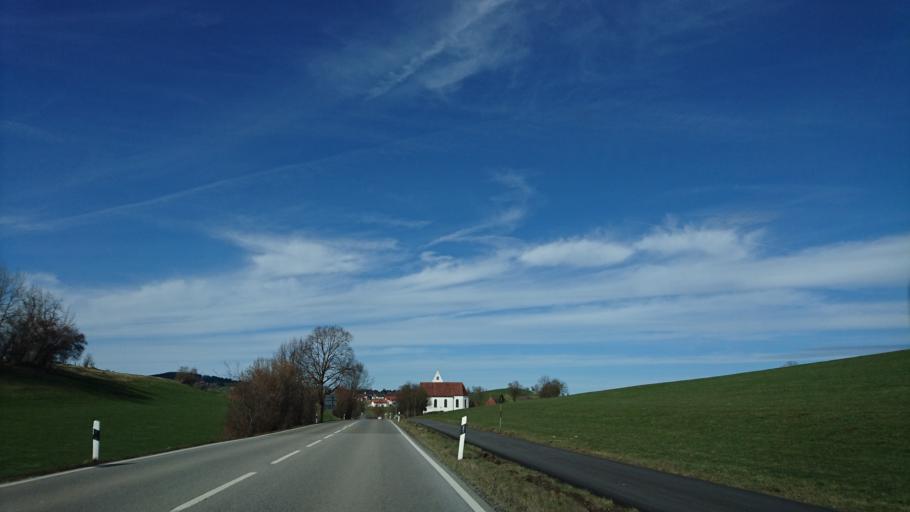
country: DE
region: Bavaria
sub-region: Swabia
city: Fuessen
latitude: 47.6052
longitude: 10.7094
